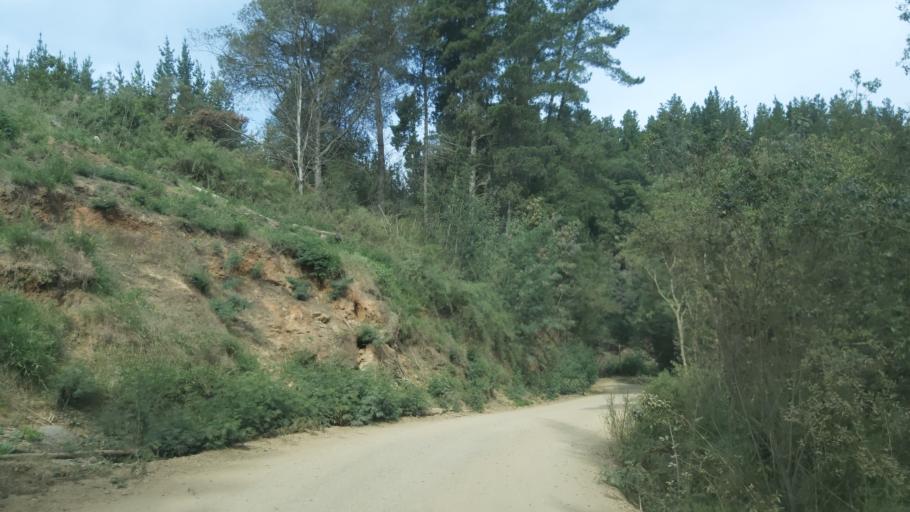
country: CL
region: Maule
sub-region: Provincia de Talca
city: Constitucion
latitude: -34.8464
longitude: -72.0399
